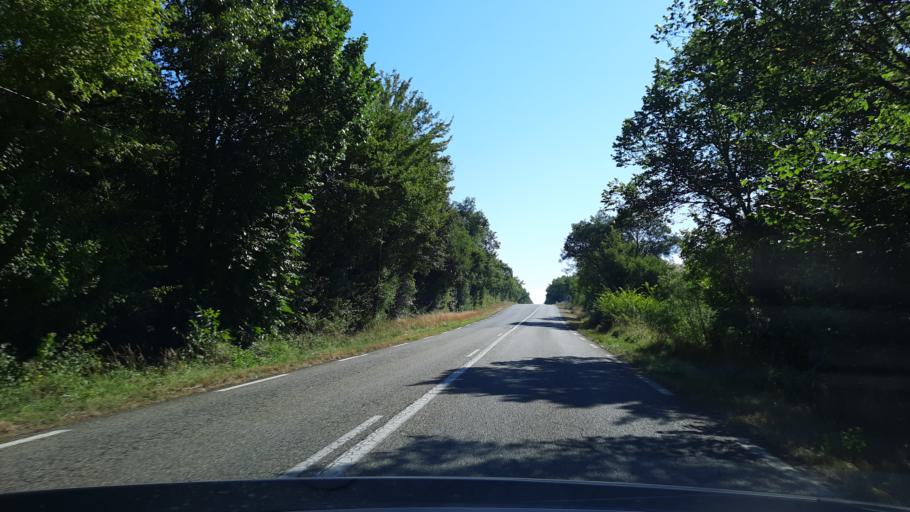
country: FR
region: Midi-Pyrenees
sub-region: Departement du Tarn-et-Garonne
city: Septfonds
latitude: 44.1847
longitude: 1.6487
